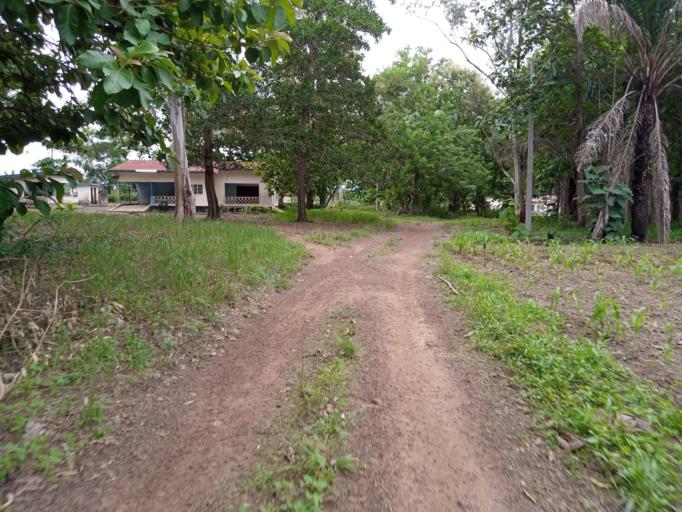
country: SL
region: Southern Province
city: Moyamba
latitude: 8.1716
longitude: -12.4198
